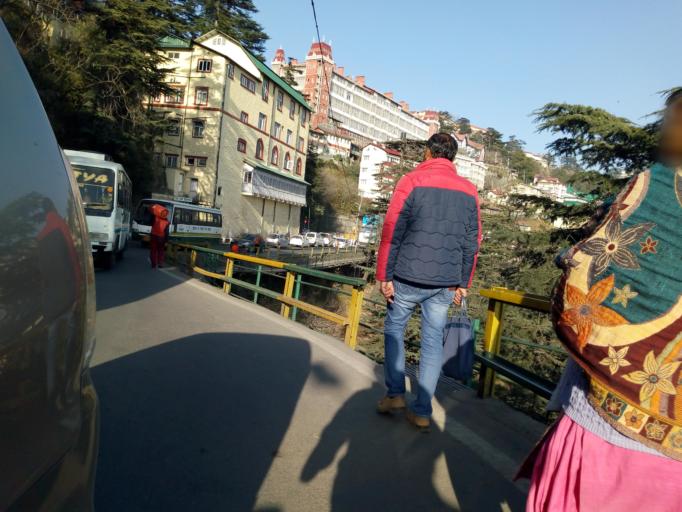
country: IN
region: Himachal Pradesh
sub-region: Shimla
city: Shimla
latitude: 31.1042
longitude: 77.1630
